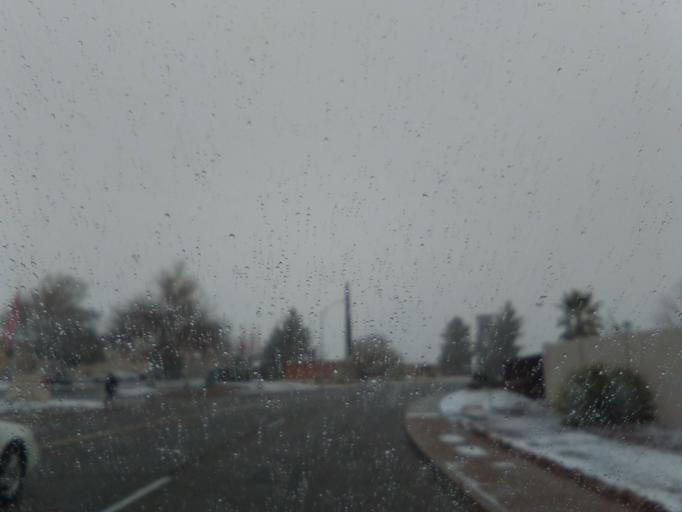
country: US
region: Arizona
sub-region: Cochise County
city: Sierra Vista
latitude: 31.5490
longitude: -110.2786
